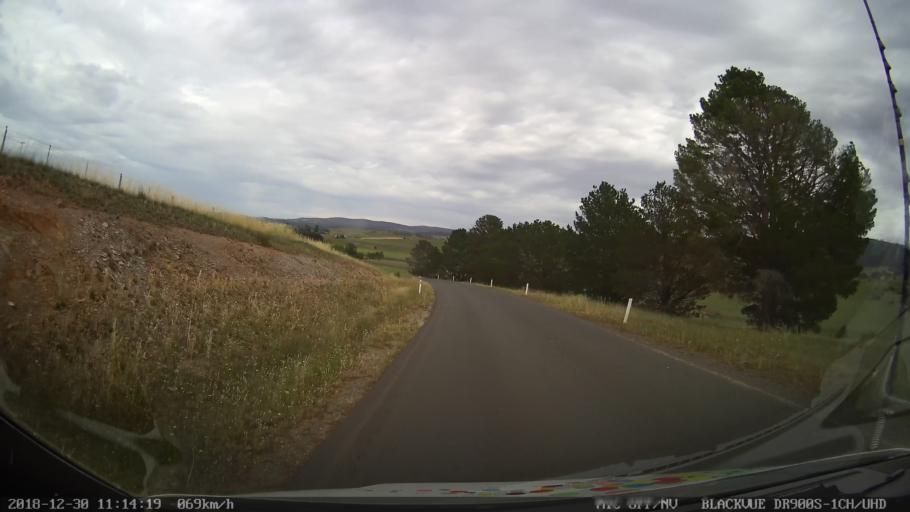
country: AU
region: New South Wales
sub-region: Snowy River
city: Jindabyne
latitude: -36.5343
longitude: 148.7307
